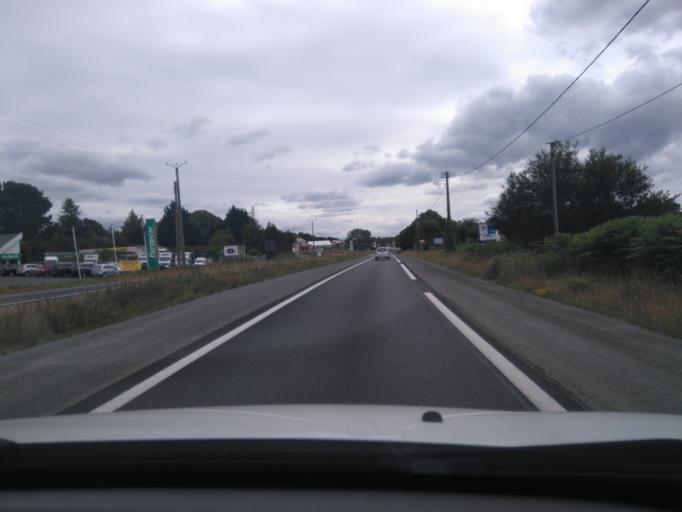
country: FR
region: Brittany
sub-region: Departement des Cotes-d'Armor
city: Saint-Quay-Perros
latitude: 48.7717
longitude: -3.4460
